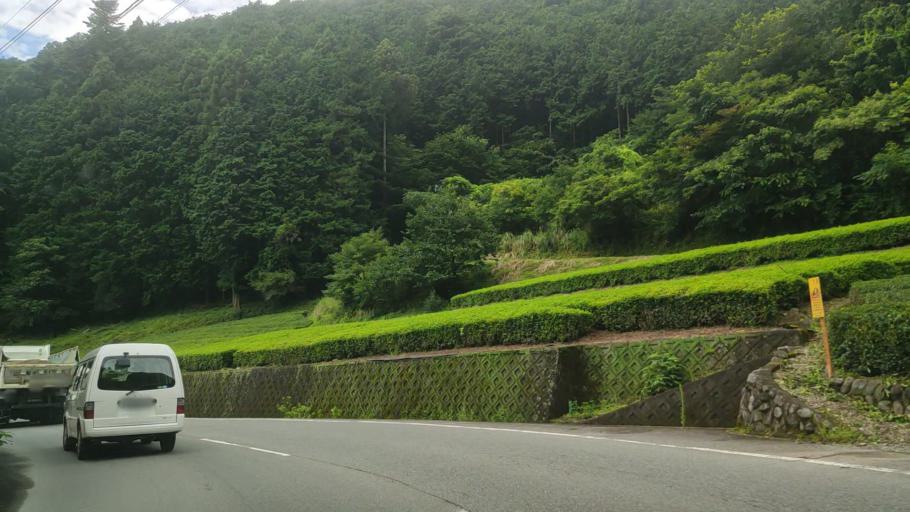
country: JP
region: Shizuoka
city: Fujinomiya
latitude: 35.2311
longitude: 138.5228
